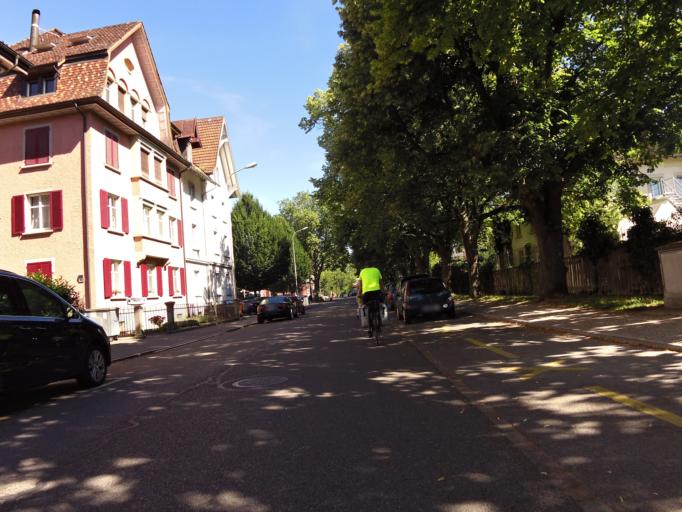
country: DE
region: Baden-Wuerttemberg
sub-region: Freiburg Region
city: Konstanz
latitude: 47.6545
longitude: 9.1756
